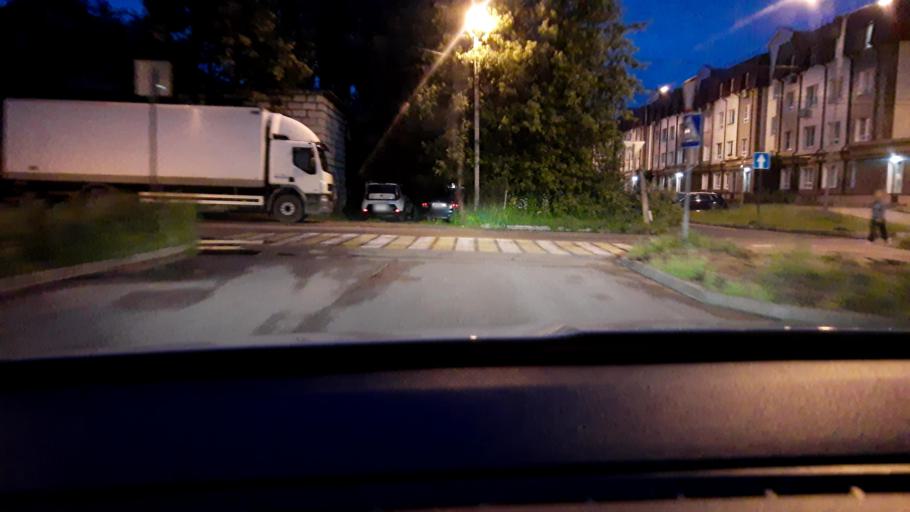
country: RU
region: Moskovskaya
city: Lesnyye Polyany
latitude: 55.9208
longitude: 37.8834
